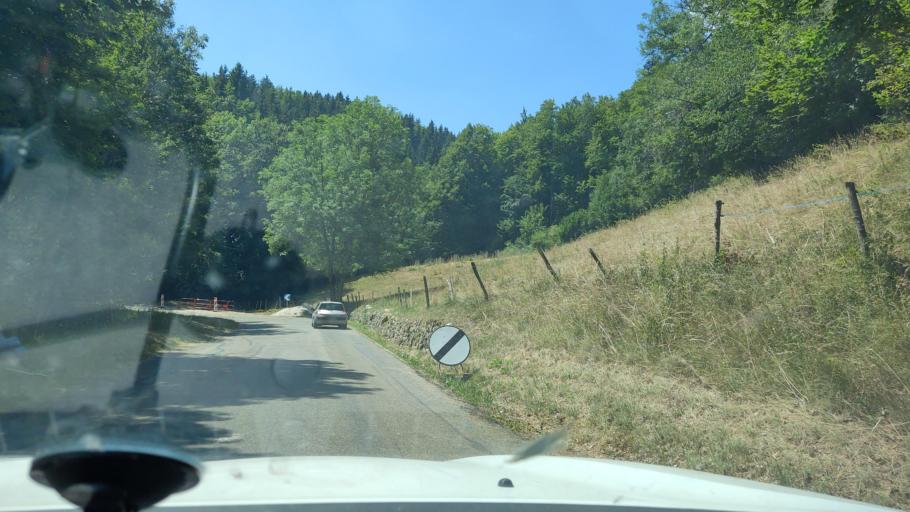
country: FR
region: Rhone-Alpes
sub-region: Departement de la Savoie
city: Mery
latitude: 45.6627
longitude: 6.0330
